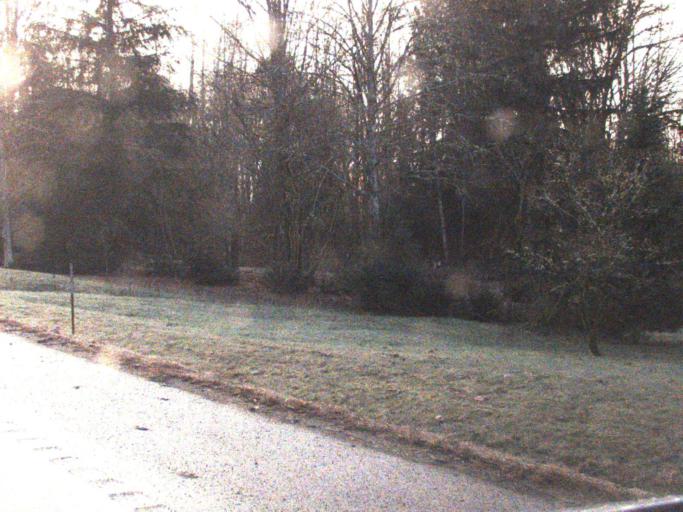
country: US
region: Washington
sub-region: Snohomish County
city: Darrington
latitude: 48.5081
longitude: -121.6573
